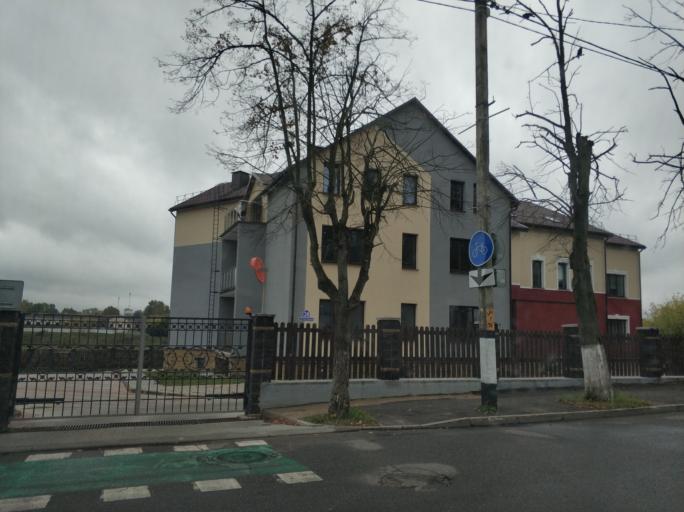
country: BY
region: Vitebsk
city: Polatsk
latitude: 55.4839
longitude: 28.7720
